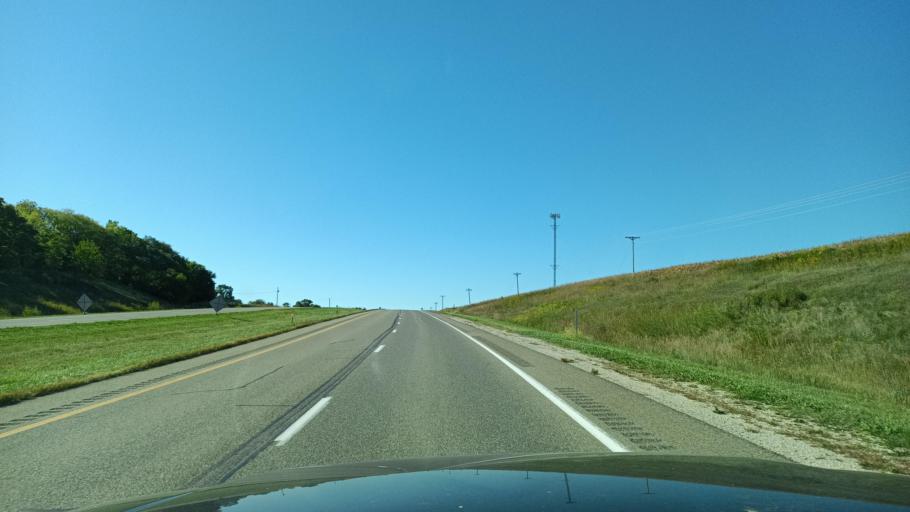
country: US
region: Iowa
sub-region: Lee County
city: Fort Madison
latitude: 40.6906
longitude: -91.2493
